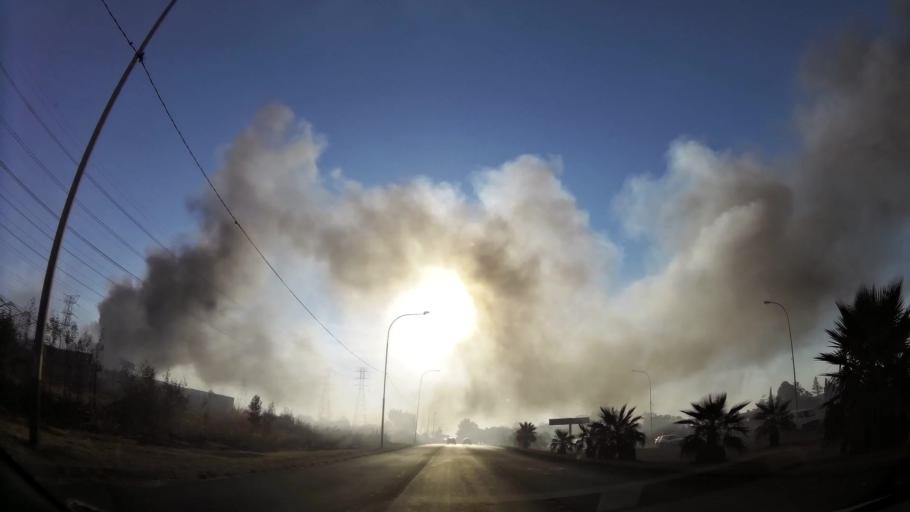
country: ZA
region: Gauteng
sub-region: City of Johannesburg Metropolitan Municipality
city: Roodepoort
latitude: -26.1763
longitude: 27.8796
